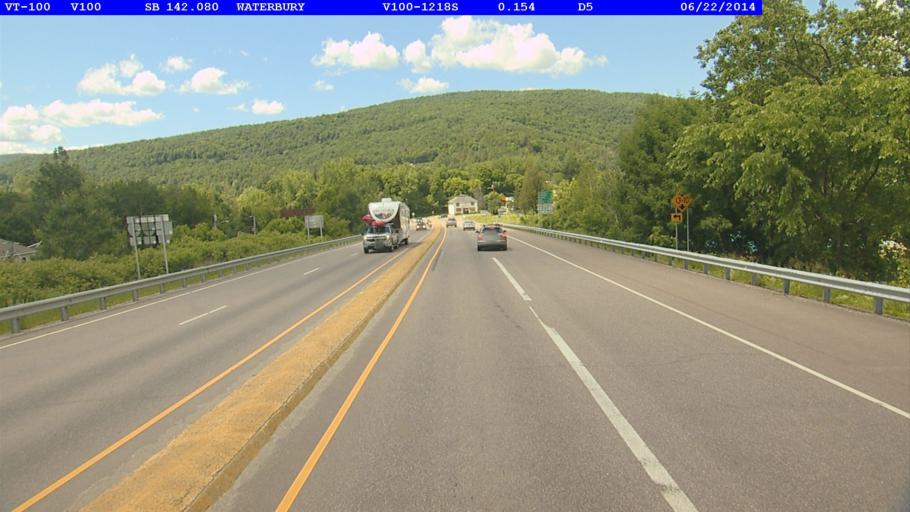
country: US
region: Vermont
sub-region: Washington County
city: Waterbury
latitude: 44.3423
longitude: -72.7568
